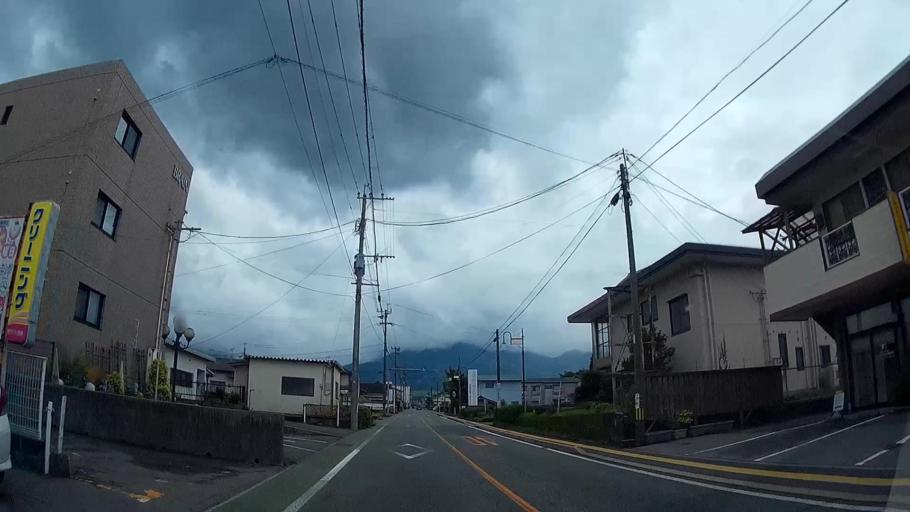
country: JP
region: Kumamoto
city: Aso
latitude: 32.9443
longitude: 131.1178
